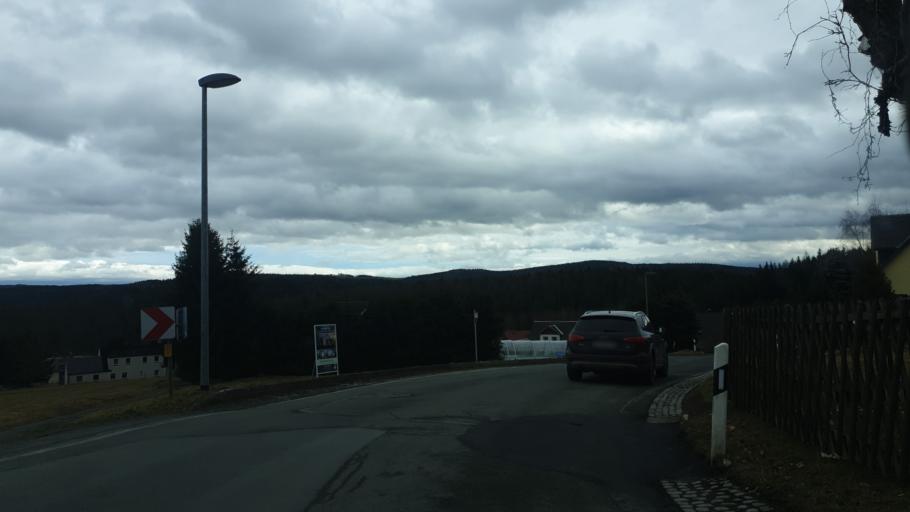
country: DE
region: Saxony
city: Bad Elster
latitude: 50.2749
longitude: 12.2784
